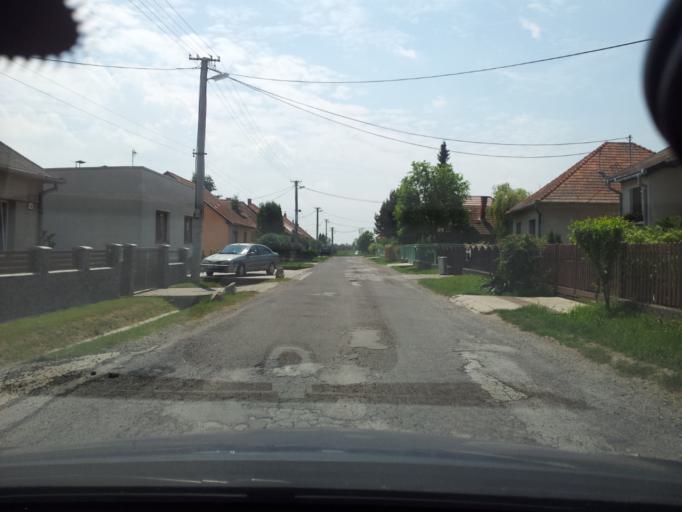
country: SK
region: Nitriansky
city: Zlate Moravce
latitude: 48.3641
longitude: 18.4143
